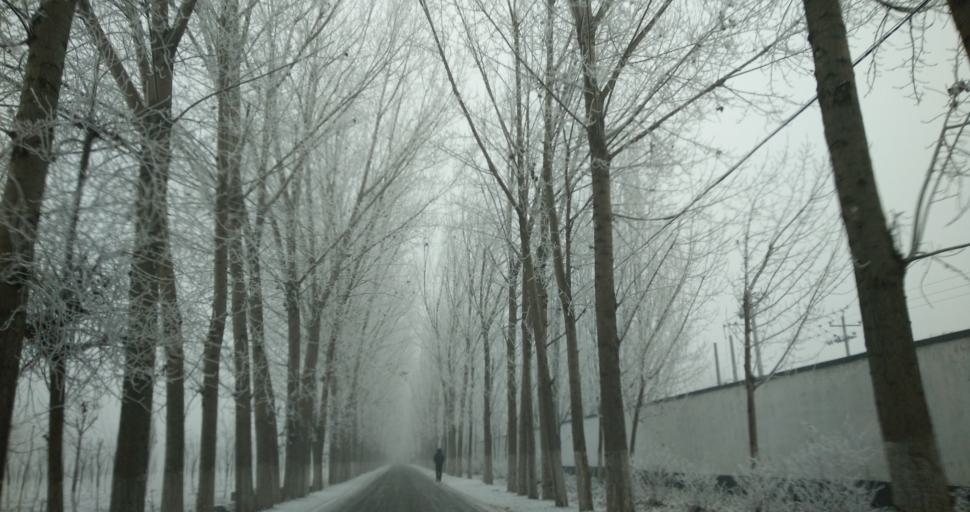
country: CN
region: Beijing
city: Yinghai
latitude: 39.7139
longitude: 116.4278
